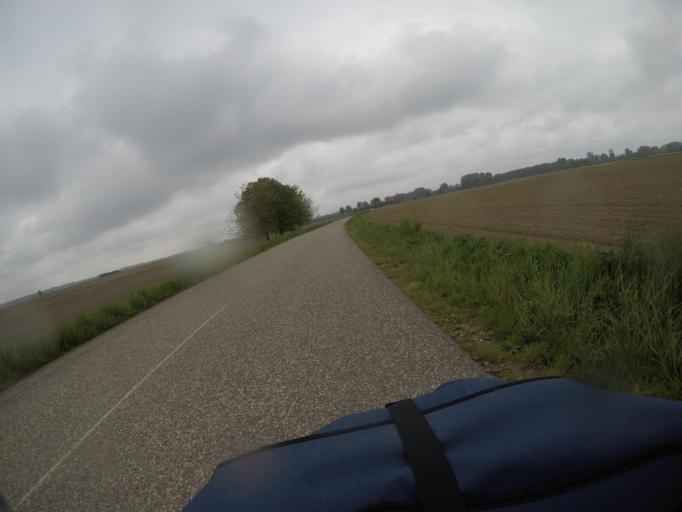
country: FR
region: Alsace
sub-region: Departement du Bas-Rhin
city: Roppenheim
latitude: 48.8238
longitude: 8.0580
